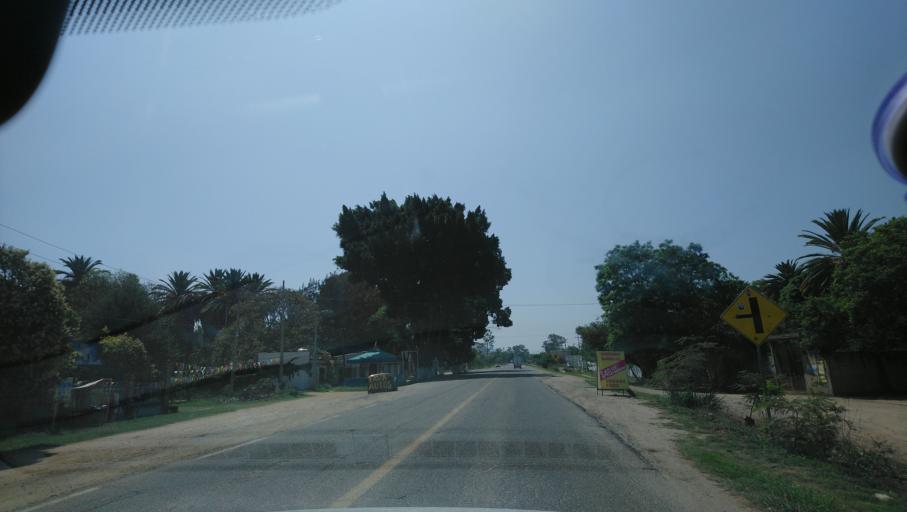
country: MX
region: Oaxaca
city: Santa Maria del Tule
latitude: 17.0443
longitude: -96.6322
